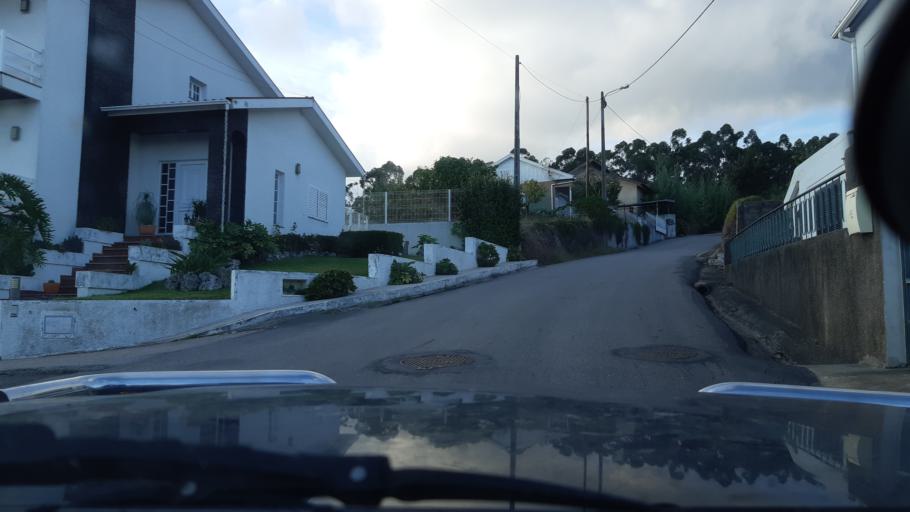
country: PT
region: Aveiro
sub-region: Agueda
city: Agueda
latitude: 40.5759
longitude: -8.4692
